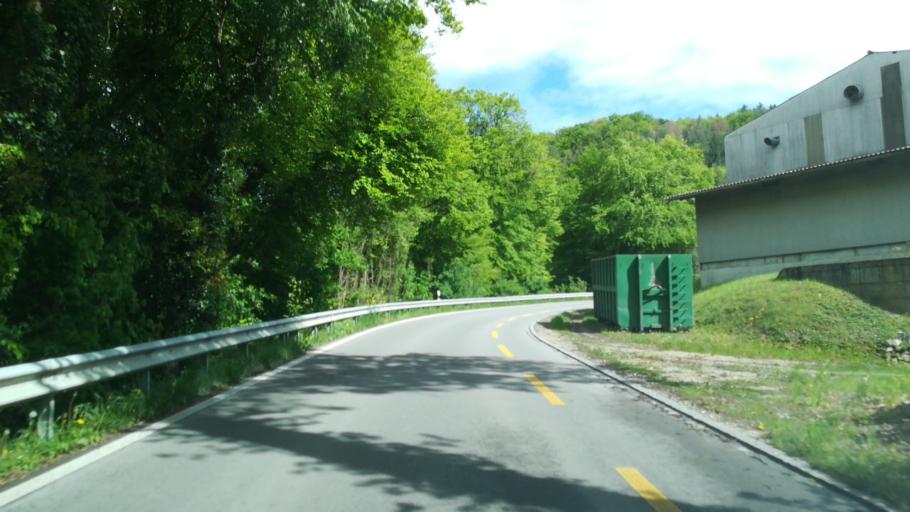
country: CH
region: Schaffhausen
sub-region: Bezirk Reiat
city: Thayngen
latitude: 47.7392
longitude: 8.7137
